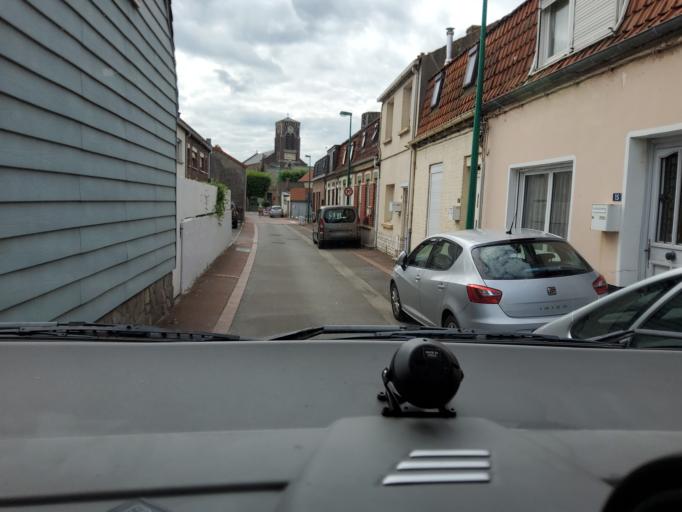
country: FR
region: Nord-Pas-de-Calais
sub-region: Departement du Nord
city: Gravelines
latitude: 50.9950
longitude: 2.1411
